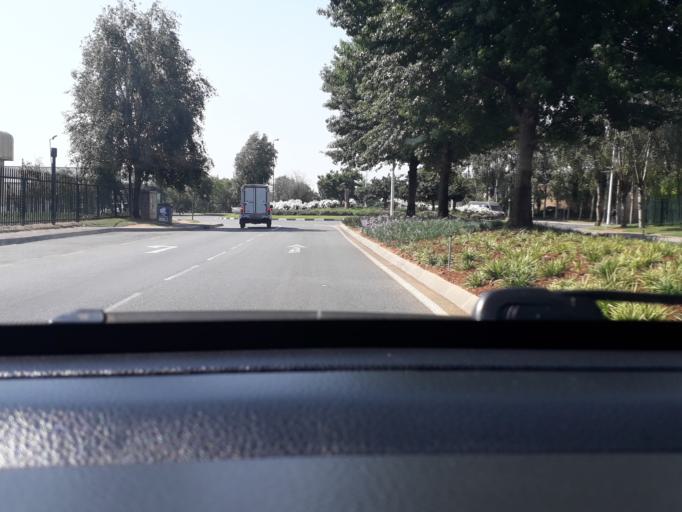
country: ZA
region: Gauteng
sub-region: City of Johannesburg Metropolitan Municipality
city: Modderfontein
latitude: -26.1128
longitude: 28.1359
